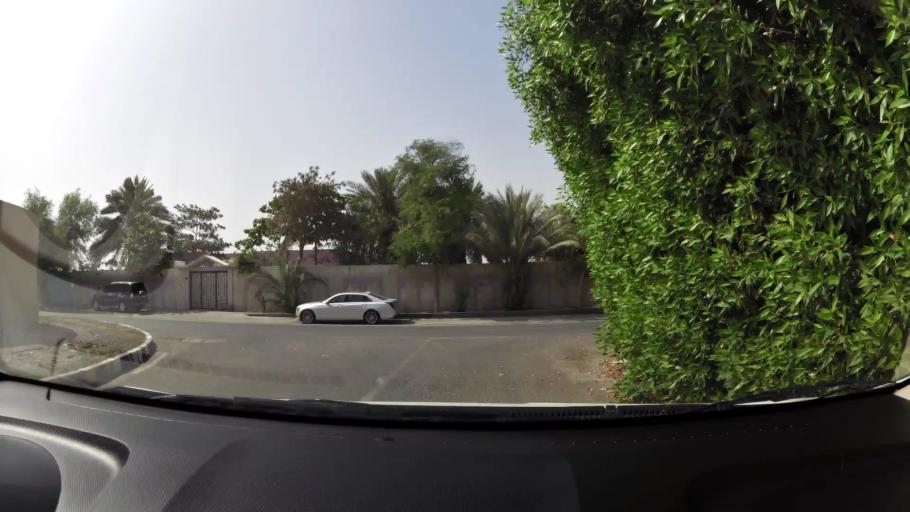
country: AE
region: Ash Shariqah
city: Sharjah
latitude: 25.3536
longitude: 55.4165
